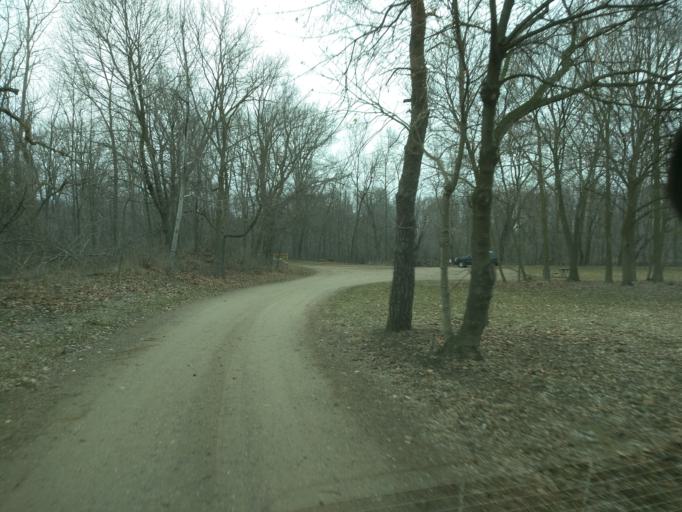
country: US
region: Michigan
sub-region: Eaton County
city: Waverly
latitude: 42.7600
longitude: -84.6125
